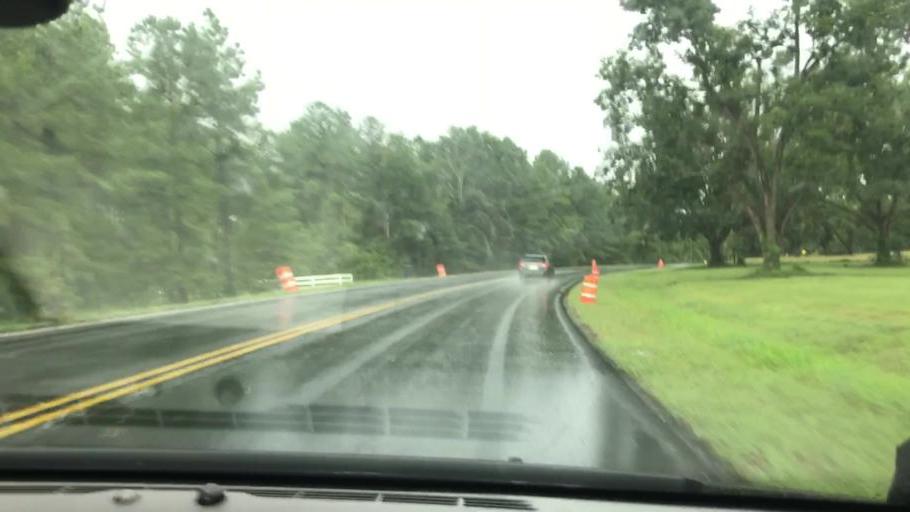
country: US
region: Georgia
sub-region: Clay County
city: Fort Gaines
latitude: 31.5712
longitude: -85.0179
